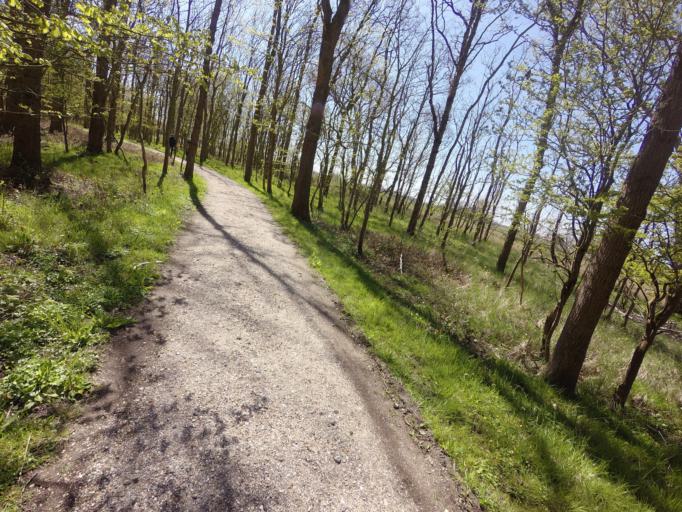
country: NL
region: Zeeland
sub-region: Gemeente Middelburg
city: Middelburg
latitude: 51.5713
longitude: 3.5316
